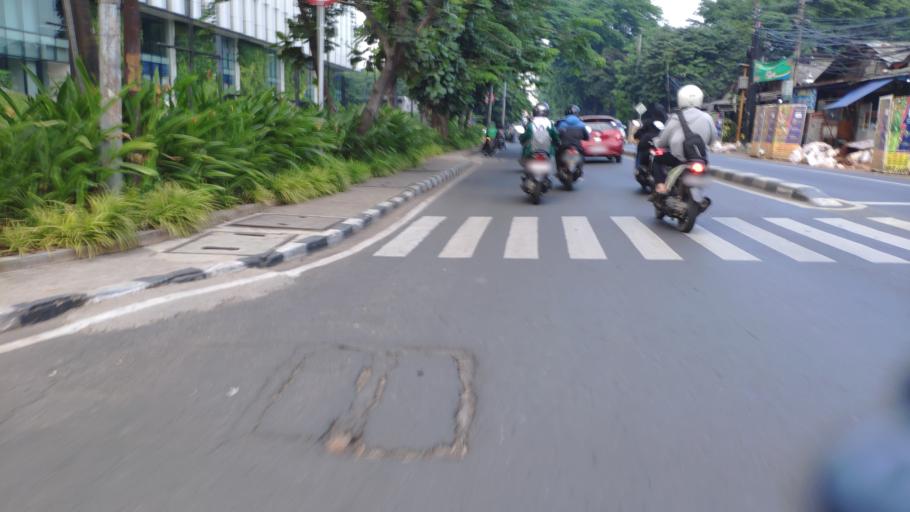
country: ID
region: Jakarta Raya
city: Jakarta
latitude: -6.2958
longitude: 106.8155
